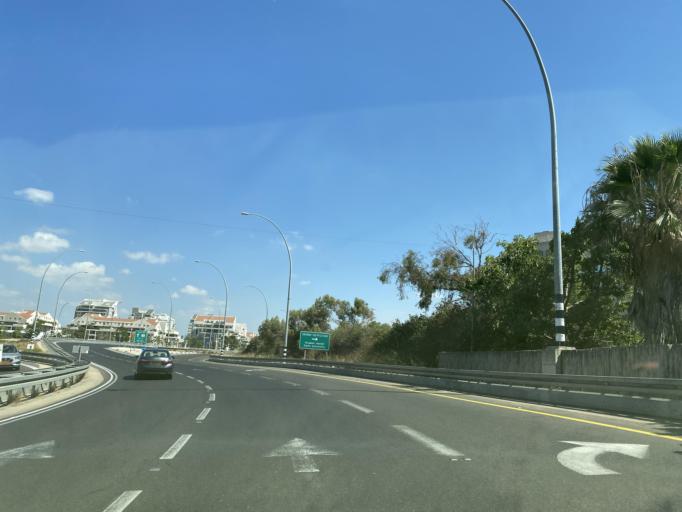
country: IL
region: Central District
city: Ra'anana
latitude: 32.1901
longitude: 34.8877
